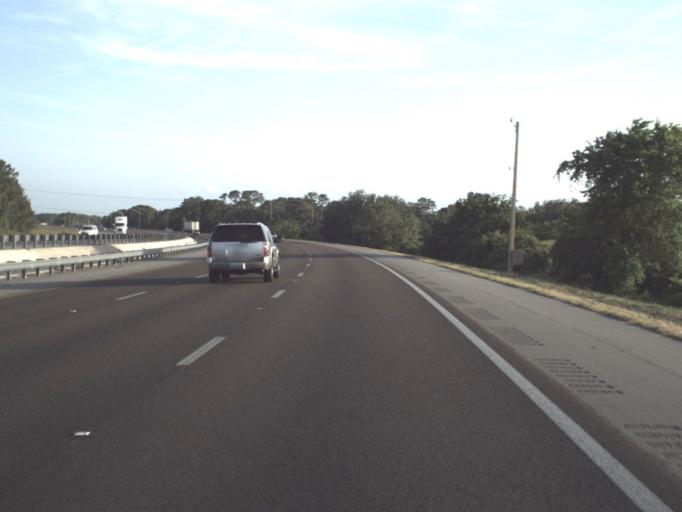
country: US
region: Florida
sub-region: Brevard County
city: Mims
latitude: 28.7186
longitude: -80.8907
